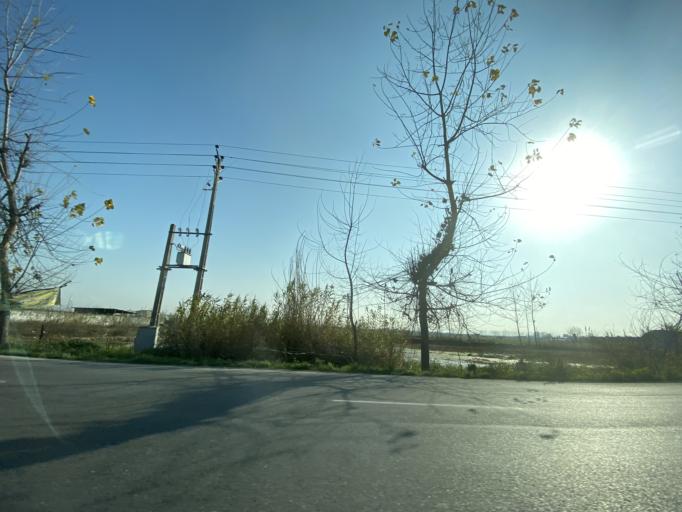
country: IR
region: Mazandaran
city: Babol
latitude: 36.5201
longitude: 52.5934
